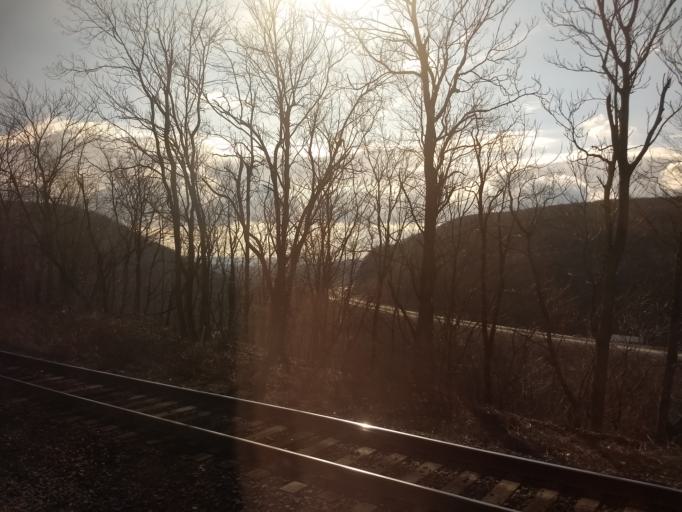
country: US
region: Pennsylvania
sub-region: Cambria County
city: Gallitzin
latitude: 40.4768
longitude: -78.5058
